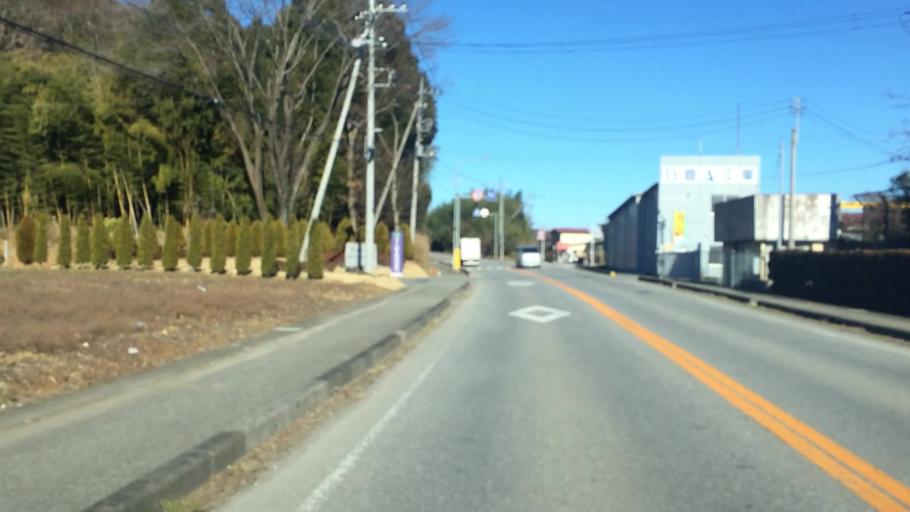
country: JP
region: Tochigi
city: Utsunomiya-shi
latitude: 36.6363
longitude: 139.8326
